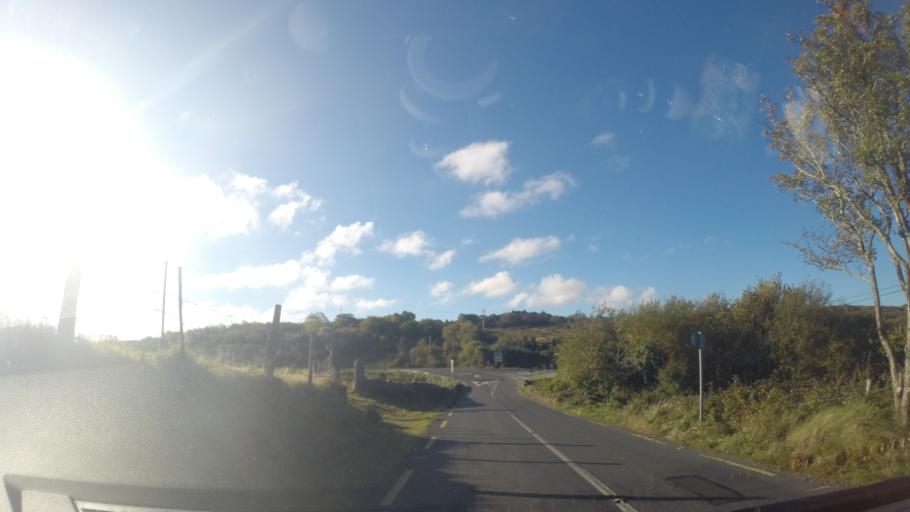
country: IE
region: Ulster
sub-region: County Donegal
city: Dungloe
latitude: 54.8312
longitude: -8.3681
